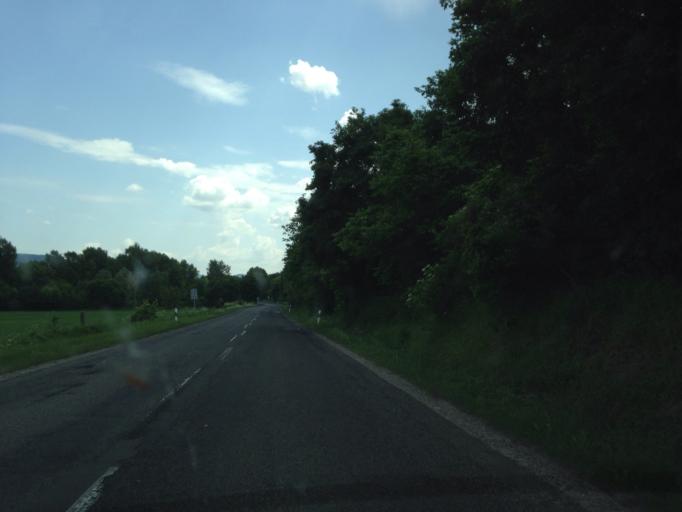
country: HU
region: Pest
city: Szob
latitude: 47.8033
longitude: 18.8510
